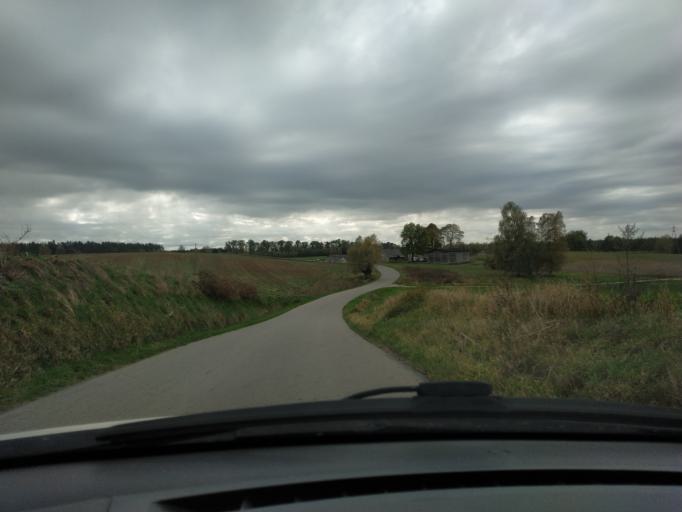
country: PL
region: Warmian-Masurian Voivodeship
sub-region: Powiat nowomiejski
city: Biskupiec
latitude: 53.4616
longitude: 19.3188
